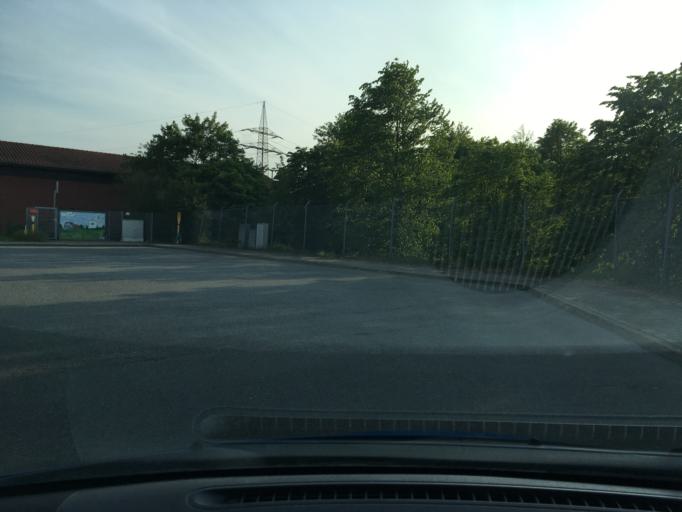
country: DE
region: Lower Saxony
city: Wendisch Evern
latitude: 53.2414
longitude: 10.4670
